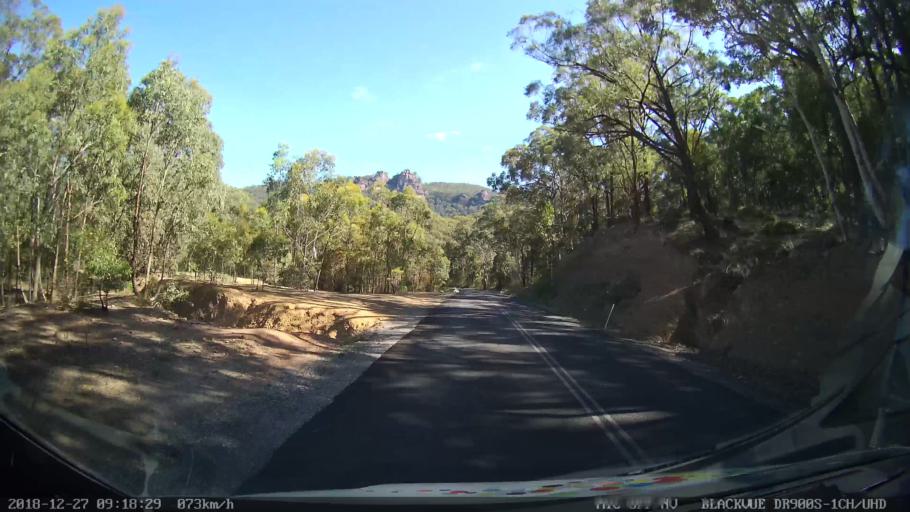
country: AU
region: New South Wales
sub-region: Lithgow
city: Portland
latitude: -33.1265
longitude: 150.0452
